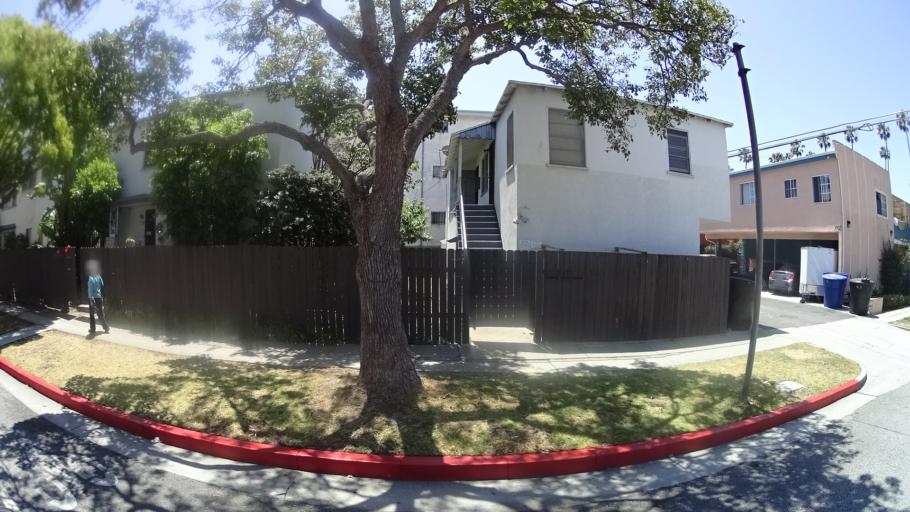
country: US
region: California
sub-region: Los Angeles County
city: Santa Monica
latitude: 34.0297
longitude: -118.4820
